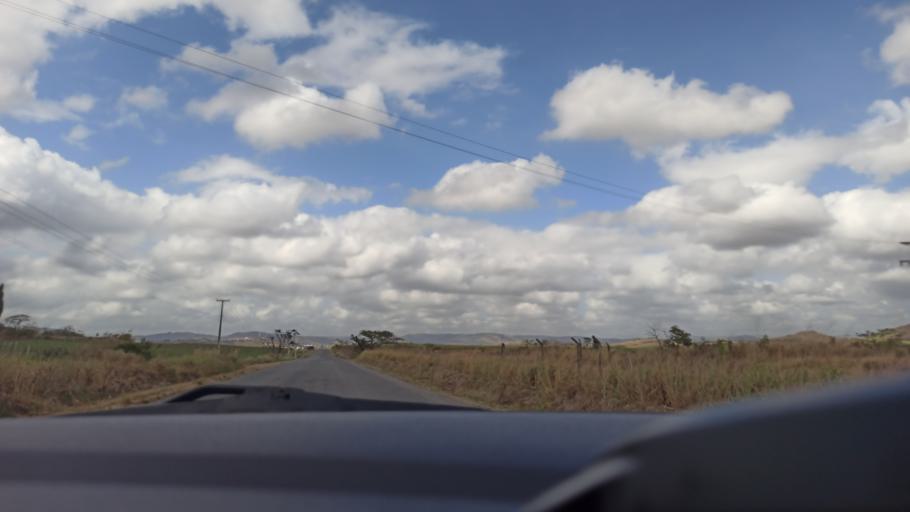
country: BR
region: Pernambuco
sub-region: Timbauba
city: Timbauba
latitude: -7.4800
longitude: -35.2853
